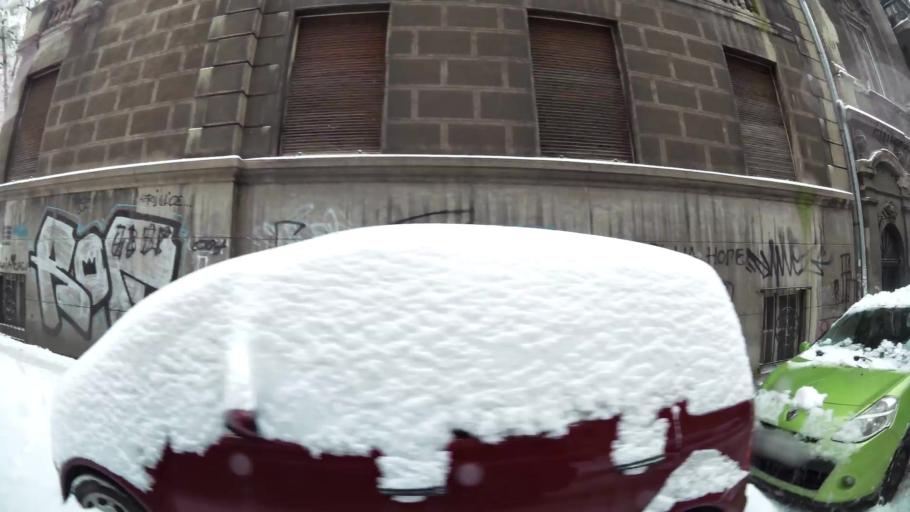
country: RS
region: Central Serbia
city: Belgrade
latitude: 44.8062
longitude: 20.4687
